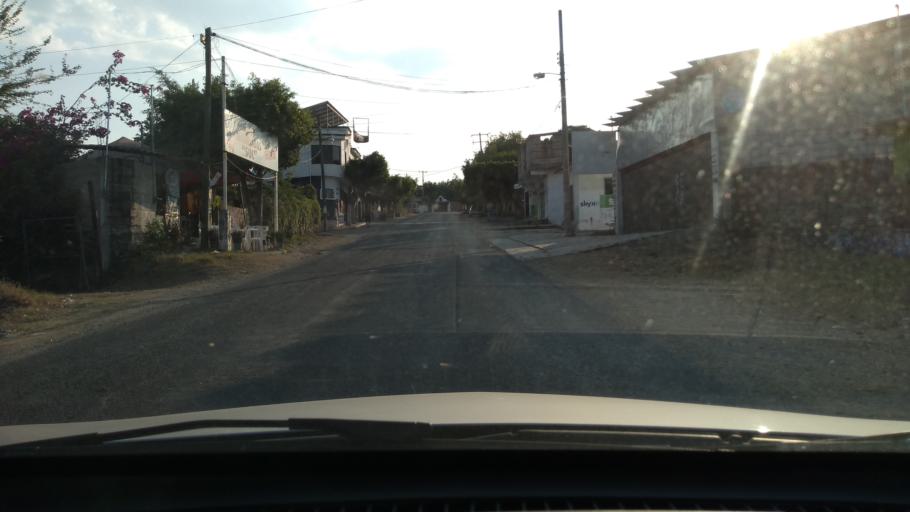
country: MX
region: Morelos
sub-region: Jojutla
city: Tehuixtla
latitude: 18.5631
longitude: -99.2728
